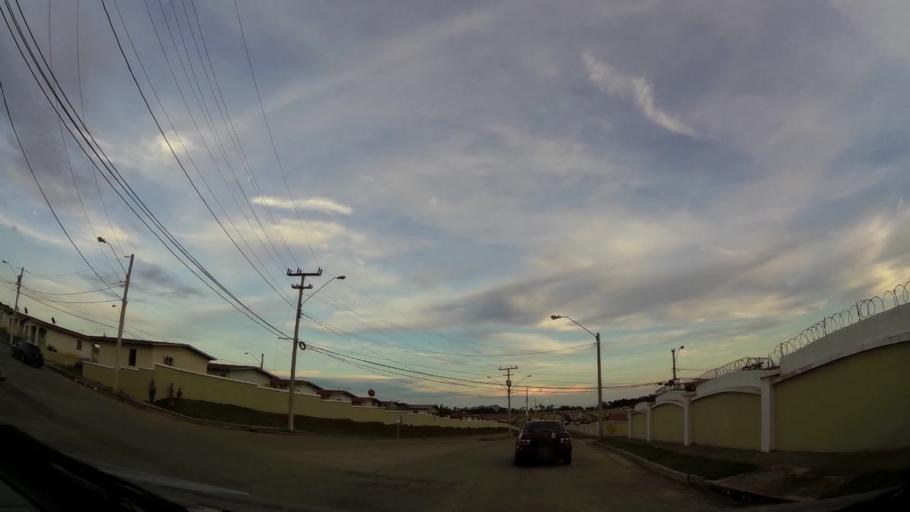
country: PA
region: Panama
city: La Chorrera
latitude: 8.8600
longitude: -79.7648
